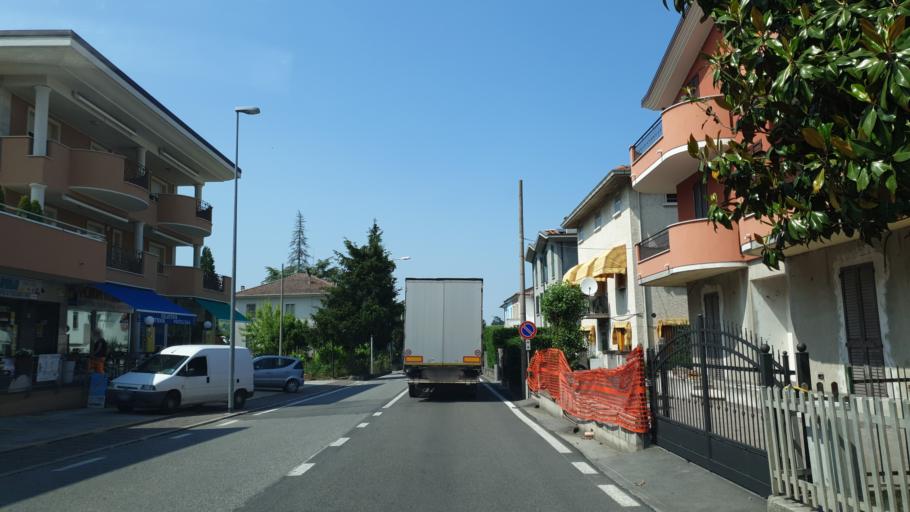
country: SM
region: Acquaviva
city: Acquaviva
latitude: 43.9526
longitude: 12.4057
